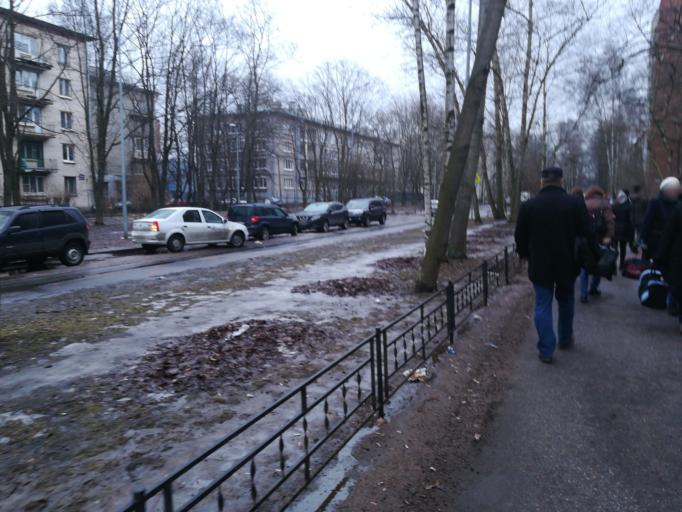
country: RU
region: St.-Petersburg
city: Vasyl'evsky Ostrov
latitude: 59.9502
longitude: 30.2407
